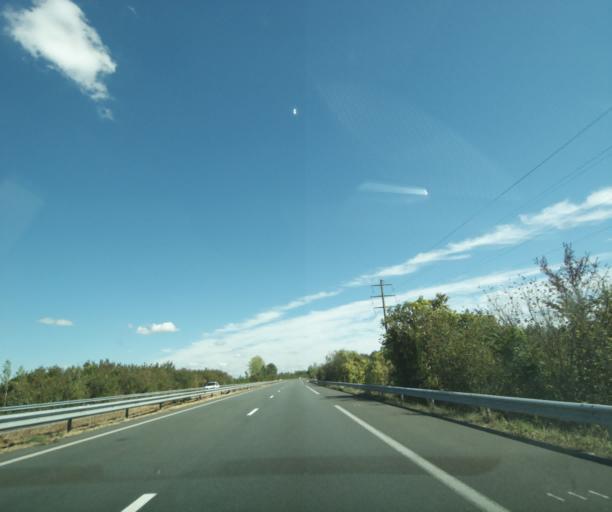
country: FR
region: Aquitaine
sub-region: Departement du Lot-et-Garonne
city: Sainte-Colombe-en-Bruilhois
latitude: 44.2116
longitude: 0.4643
